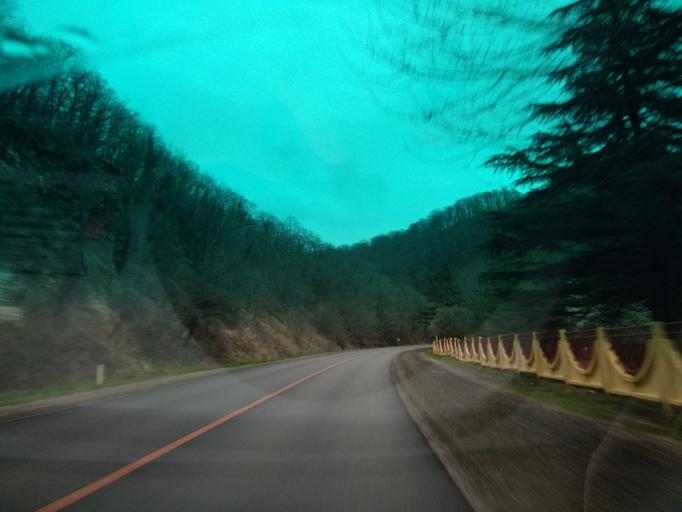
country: RU
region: Krasnodarskiy
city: Novomikhaylovskiy
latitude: 44.2593
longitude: 38.8279
